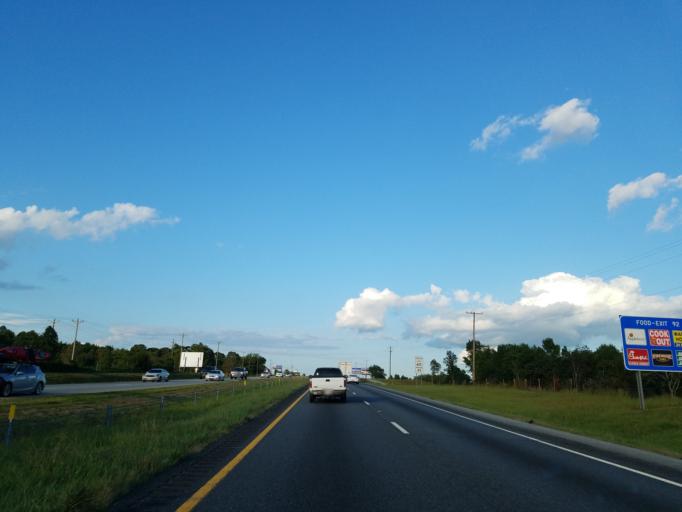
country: US
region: South Carolina
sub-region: Cherokee County
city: Gaffney
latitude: 35.0879
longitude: -81.6964
